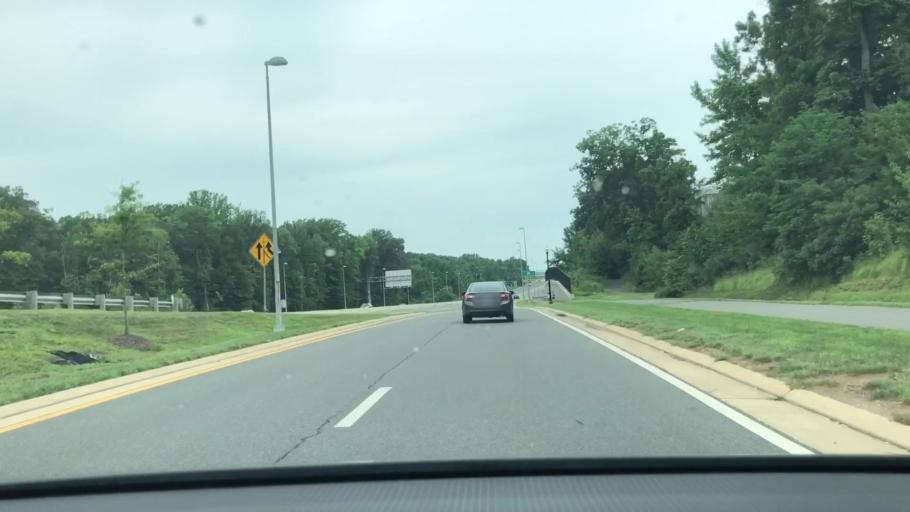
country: US
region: Virginia
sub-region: Fairfax County
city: Greenbriar
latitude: 38.8665
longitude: -77.3821
